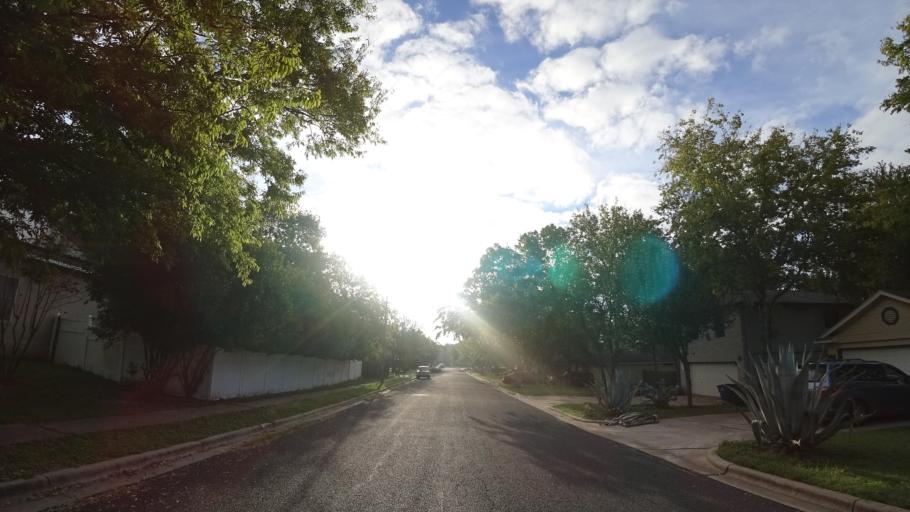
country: US
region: Texas
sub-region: Travis County
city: Onion Creek
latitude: 30.1896
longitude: -97.7369
